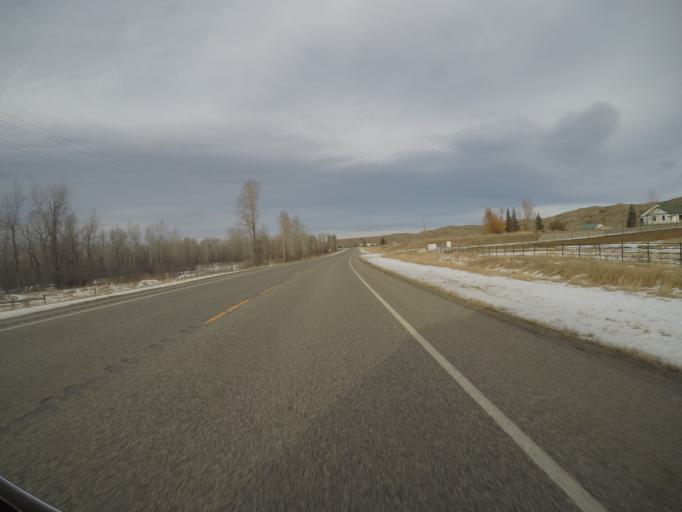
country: US
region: Montana
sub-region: Stillwater County
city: Absarokee
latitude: 45.4612
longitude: -109.4489
